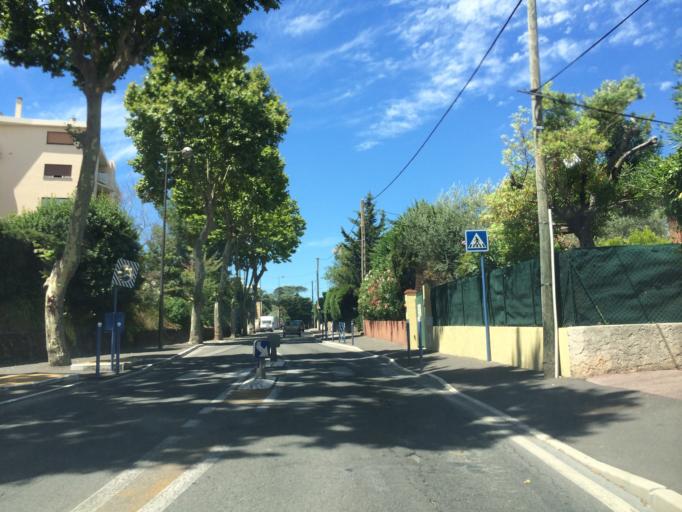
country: FR
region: Provence-Alpes-Cote d'Azur
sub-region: Departement des Alpes-Maritimes
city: Cagnes-sur-Mer
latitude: 43.6598
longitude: 7.1578
